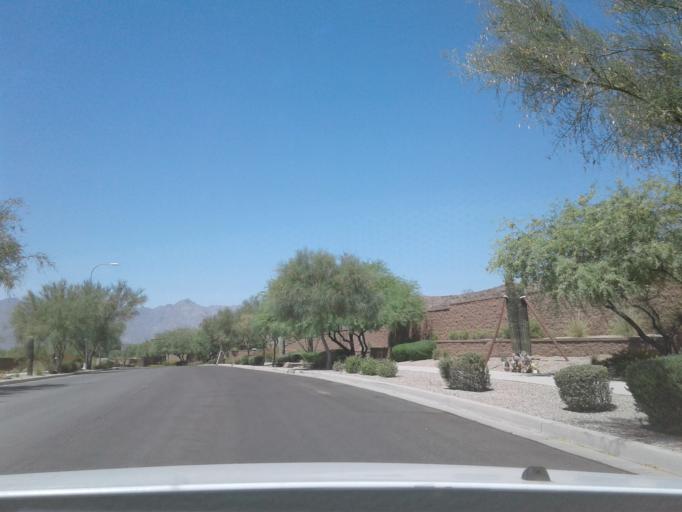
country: US
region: Arizona
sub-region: Maricopa County
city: Laveen
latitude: 33.2959
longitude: -112.1276
